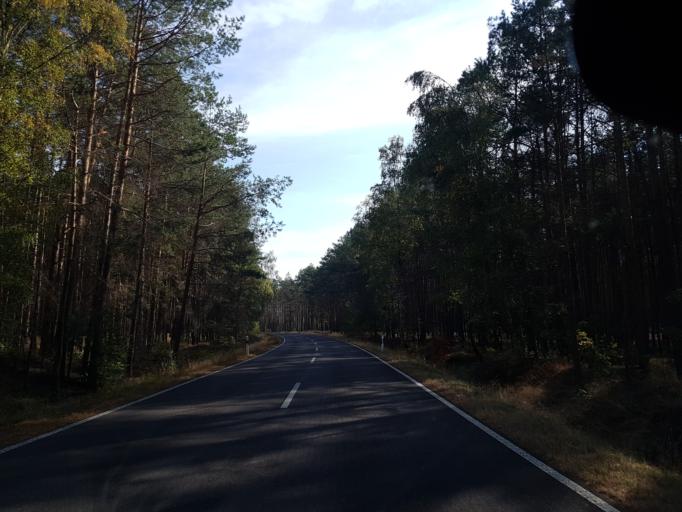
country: DE
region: Brandenburg
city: Schonborn
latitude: 51.6794
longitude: 13.4649
